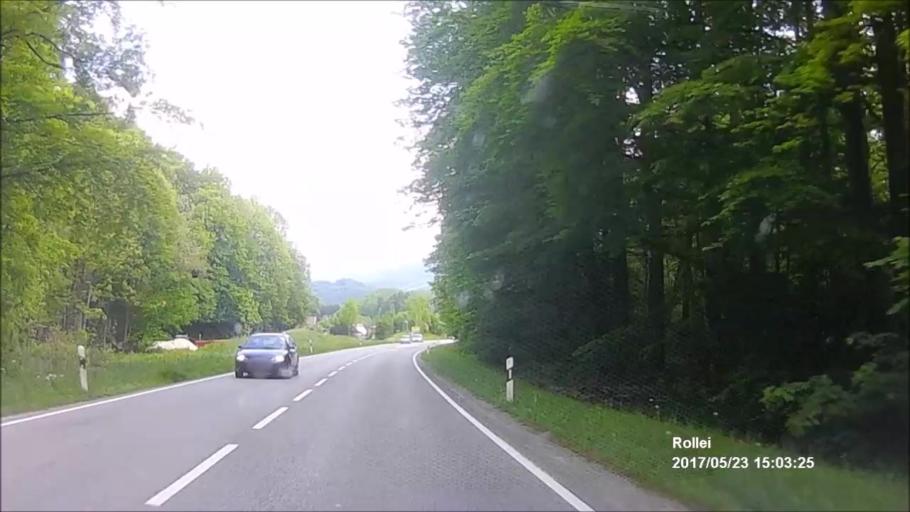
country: DE
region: Bavaria
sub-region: Upper Bavaria
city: Siegsdorf
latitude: 47.8331
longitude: 12.6469
